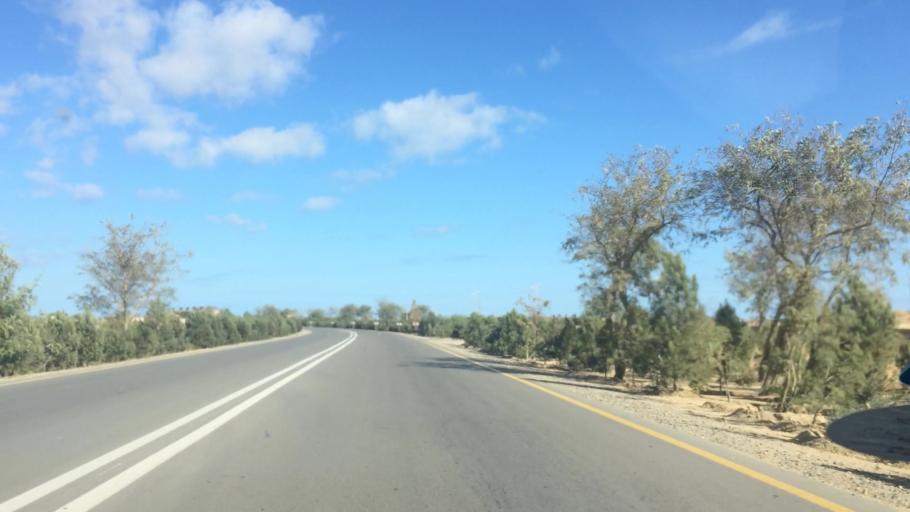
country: AZ
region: Baki
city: Pirallahi
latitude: 40.4214
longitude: 50.3562
